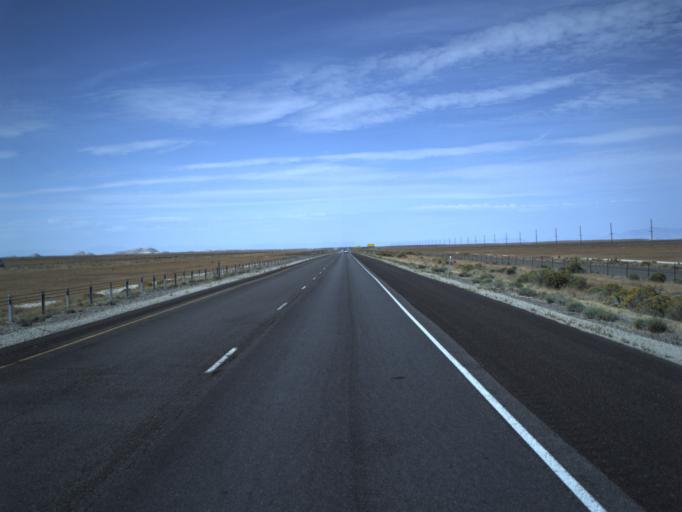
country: US
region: Utah
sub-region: Tooele County
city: Grantsville
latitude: 40.7261
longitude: -113.1522
